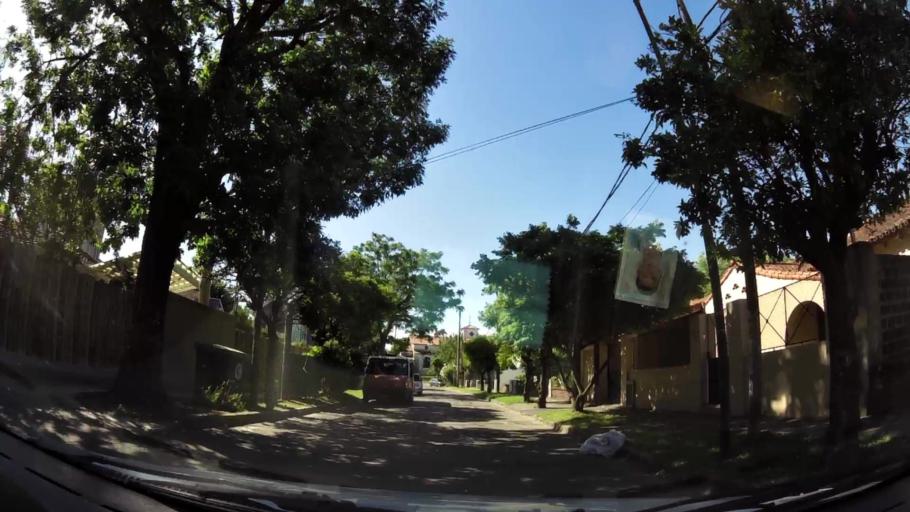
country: AR
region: Buenos Aires
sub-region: Partido de San Isidro
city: San Isidro
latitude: -34.4721
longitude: -58.5305
